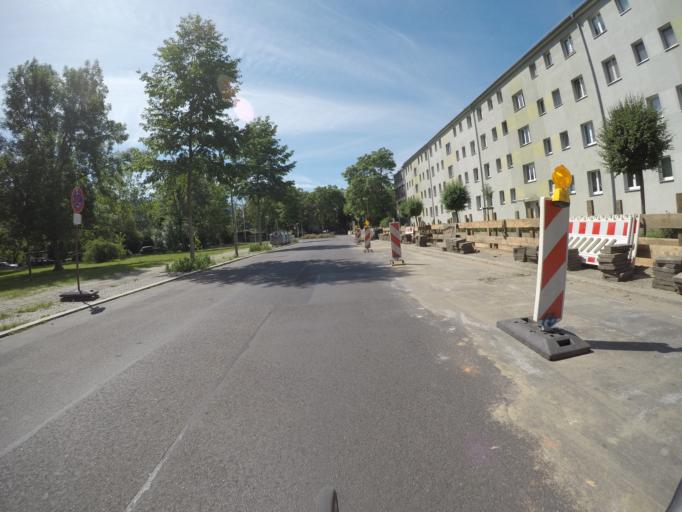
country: DE
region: Berlin
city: Friedrichsfelde
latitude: 52.5050
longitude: 13.5113
